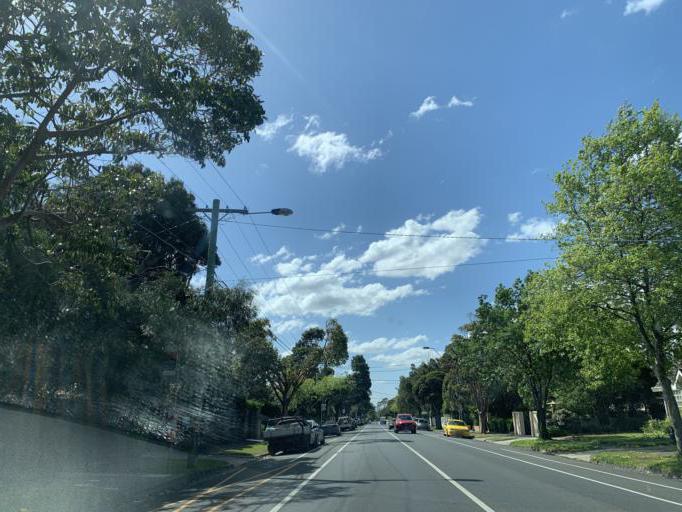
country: AU
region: Victoria
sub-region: Bayside
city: North Brighton
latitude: -37.9187
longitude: 144.9929
